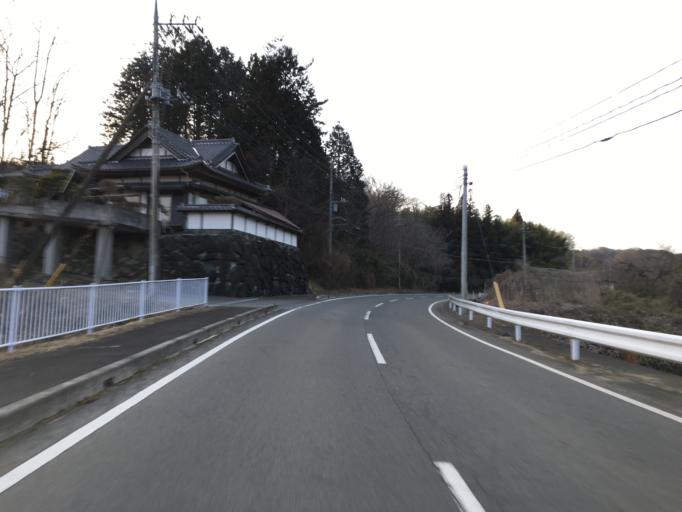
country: JP
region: Ibaraki
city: Daigo
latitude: 36.7903
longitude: 140.4142
